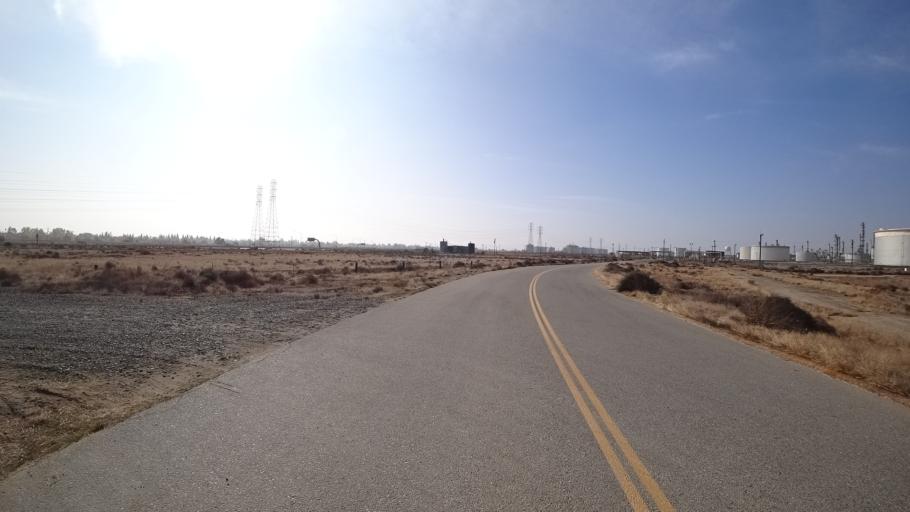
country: US
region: California
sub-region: Kern County
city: Greenacres
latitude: 35.3724
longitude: -119.0689
